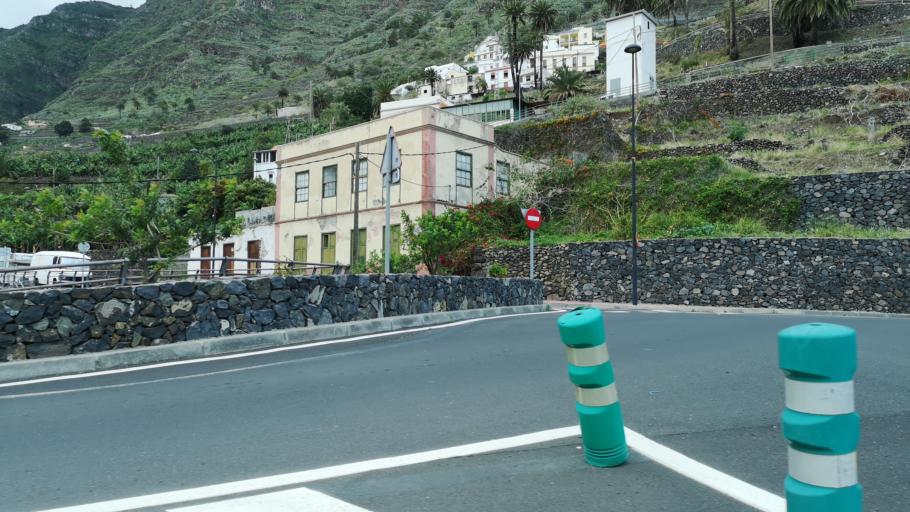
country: ES
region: Canary Islands
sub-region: Provincia de Santa Cruz de Tenerife
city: Hermigua
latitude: 28.1699
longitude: -17.1918
